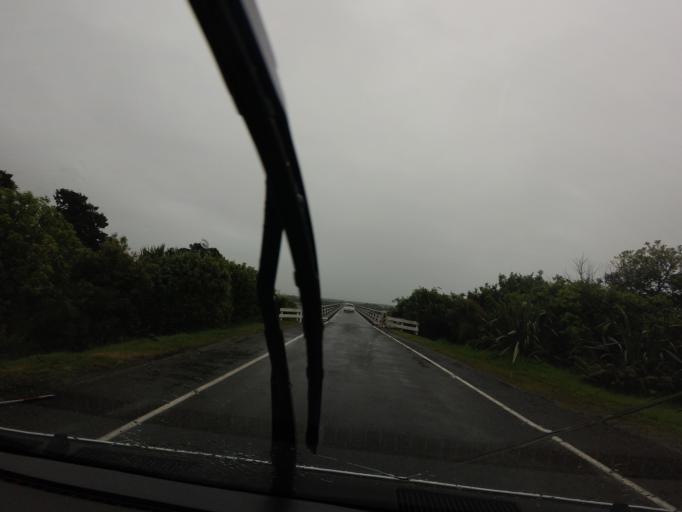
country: NZ
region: Otago
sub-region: Queenstown-Lakes District
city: Wanaka
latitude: -43.8542
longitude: 169.0550
